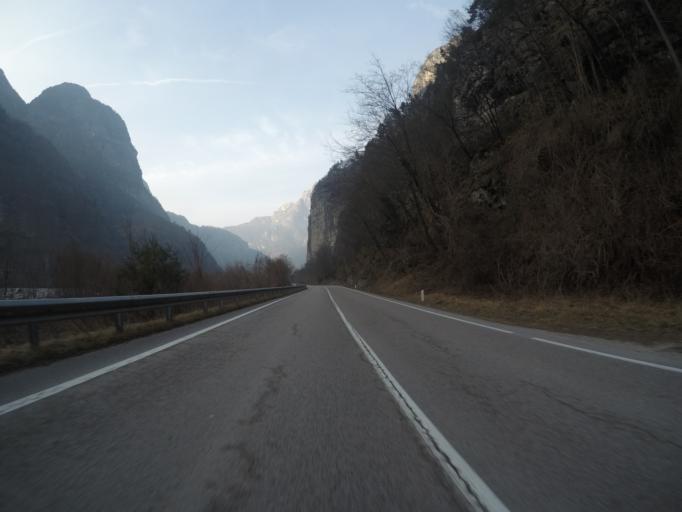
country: IT
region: Veneto
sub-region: Provincia di Belluno
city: La Valle Agordina
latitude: 46.2276
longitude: 12.1162
